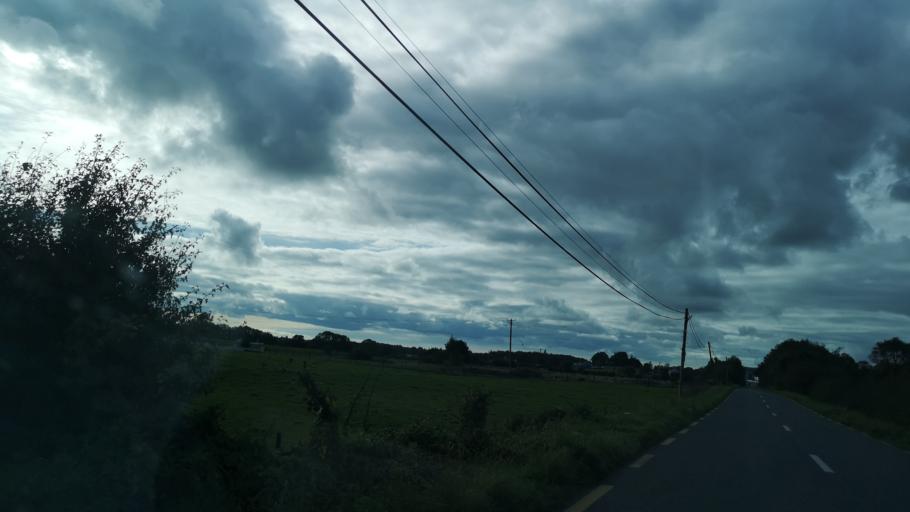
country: IE
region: Connaught
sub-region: County Galway
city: Ballinasloe
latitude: 53.2918
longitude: -8.0938
